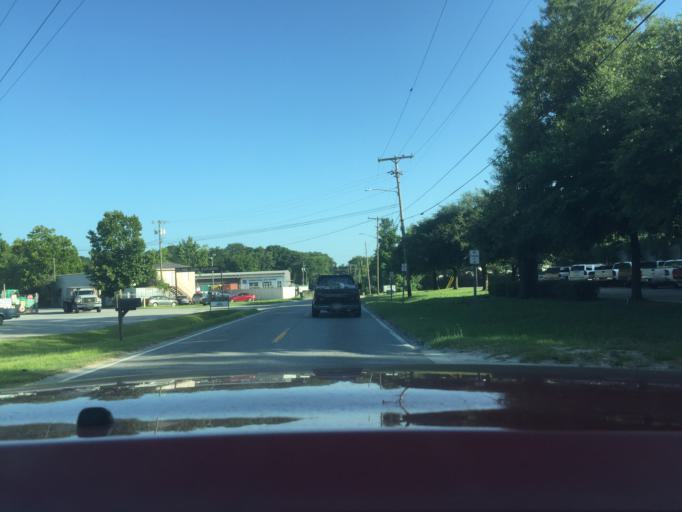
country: US
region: Georgia
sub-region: Chatham County
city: Savannah
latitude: 32.0573
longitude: -81.1333
